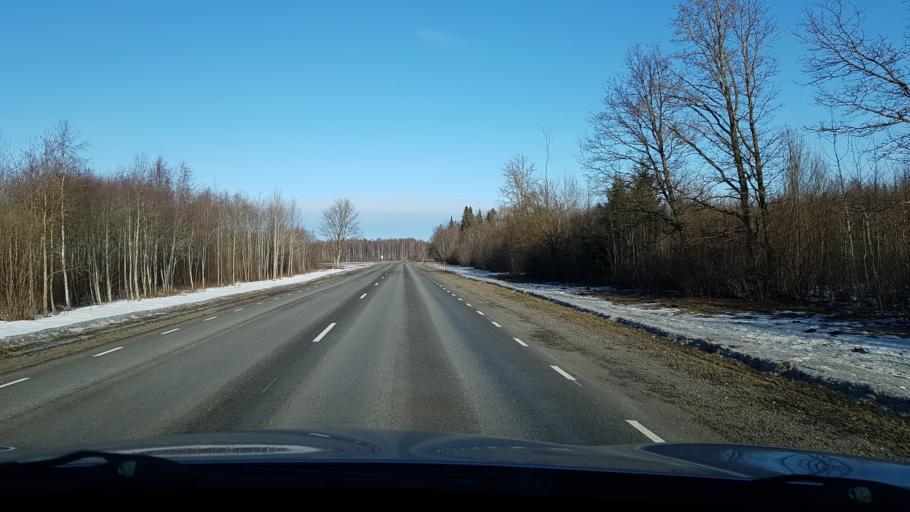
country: EE
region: Viljandimaa
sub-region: Vohma linn
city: Vohma
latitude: 58.6170
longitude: 25.5700
